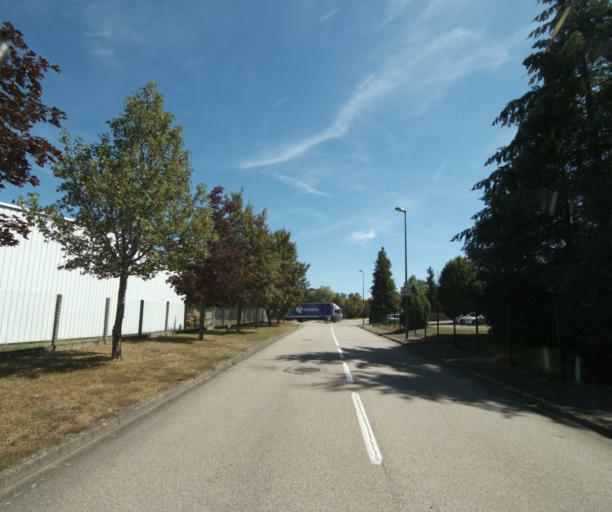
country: FR
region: Lorraine
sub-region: Departement des Vosges
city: Dogneville
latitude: 48.2039
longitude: 6.4578
